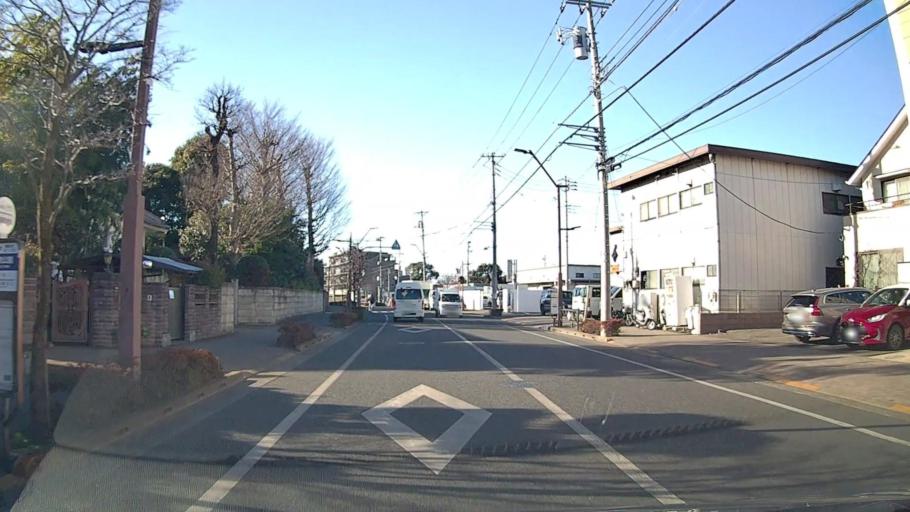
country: JP
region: Tokyo
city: Chofugaoka
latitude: 35.6599
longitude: 139.5590
